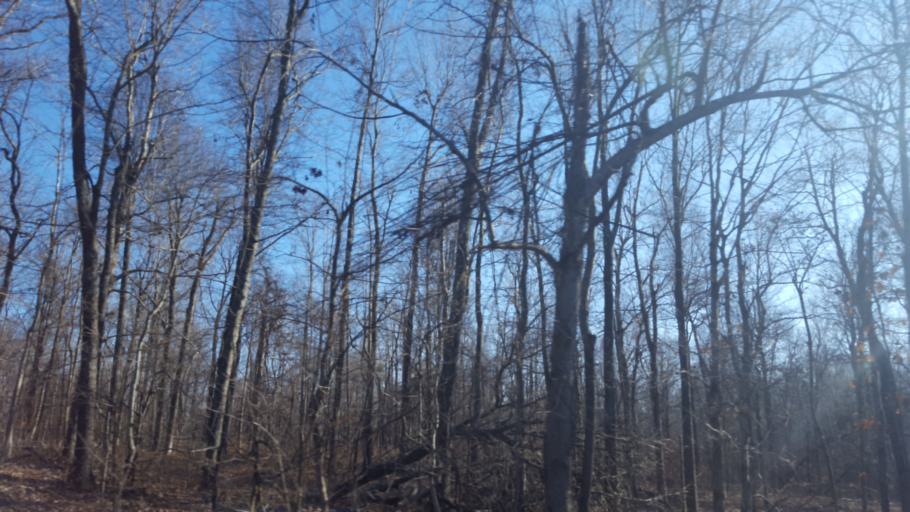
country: US
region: Kentucky
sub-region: Crittenden County
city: Marion
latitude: 37.4501
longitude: -88.0760
